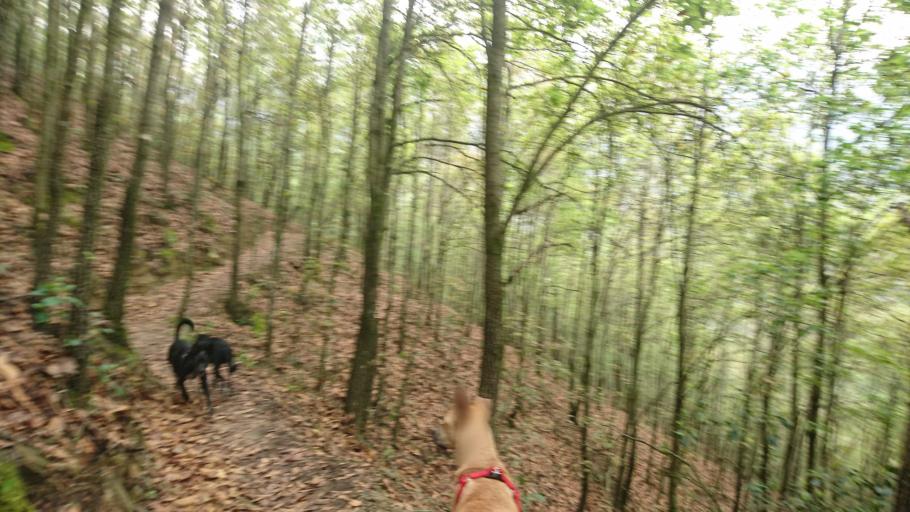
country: MX
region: Nuevo Leon
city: Garza Garcia
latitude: 25.6017
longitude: -100.3348
